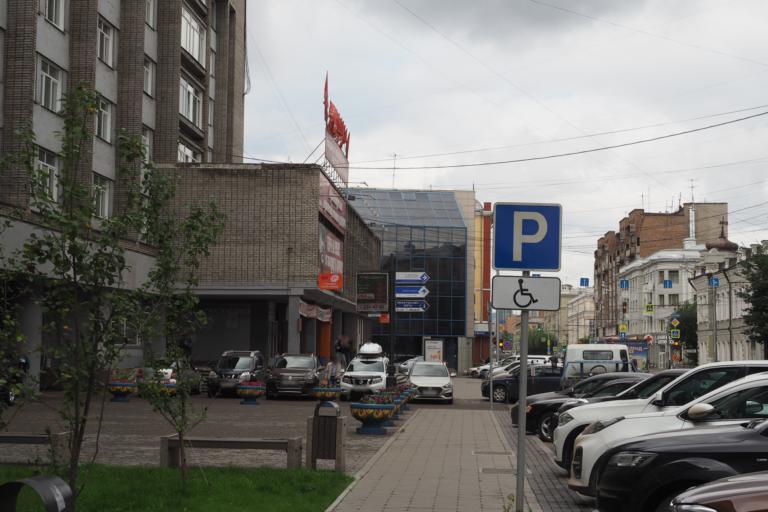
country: RU
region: Krasnoyarskiy
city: Krasnoyarsk
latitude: 56.0130
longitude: 92.8613
